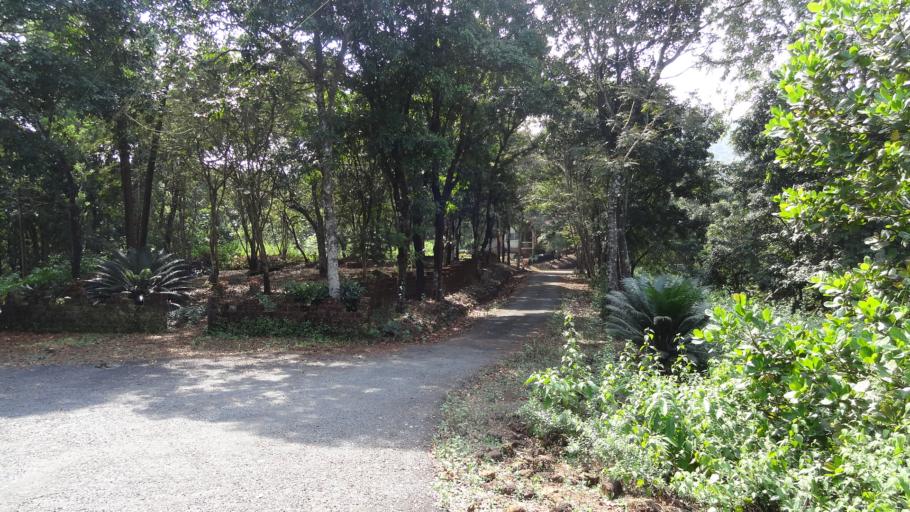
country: IN
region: Goa
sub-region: North Goa
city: Palle
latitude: 15.4372
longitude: 74.1035
